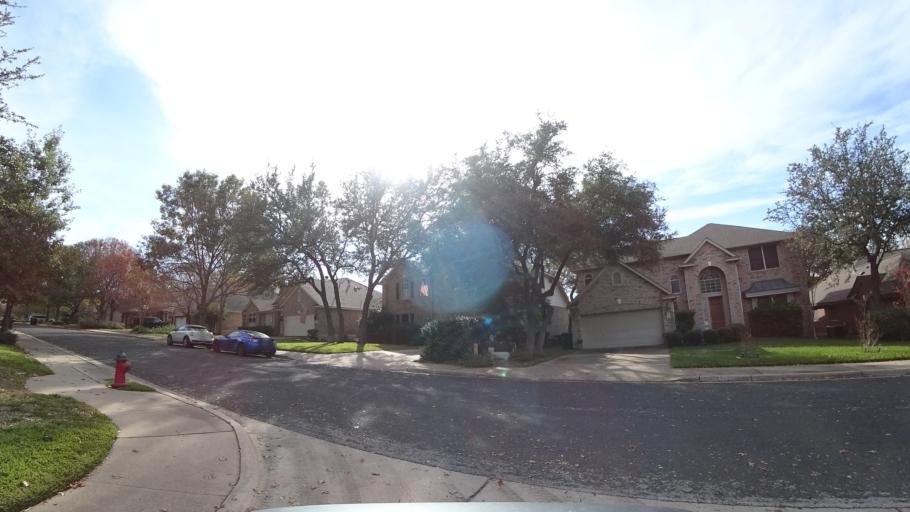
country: US
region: Texas
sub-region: Williamson County
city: Brushy Creek
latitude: 30.5121
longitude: -97.7461
